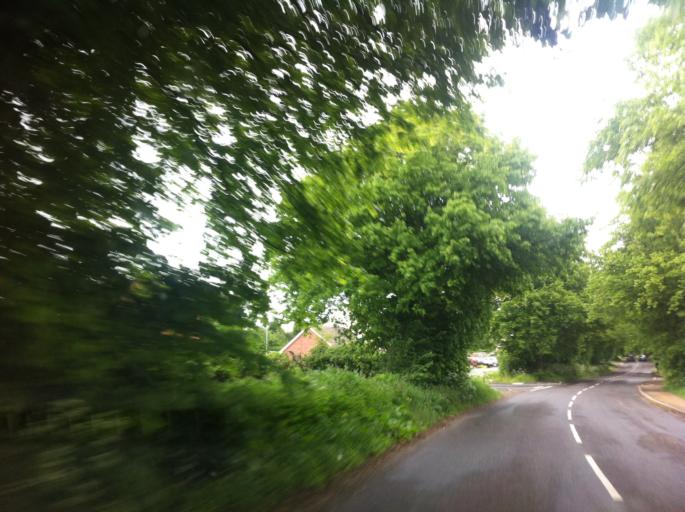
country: GB
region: England
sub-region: Northamptonshire
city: Earls Barton
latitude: 52.2703
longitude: -0.7203
